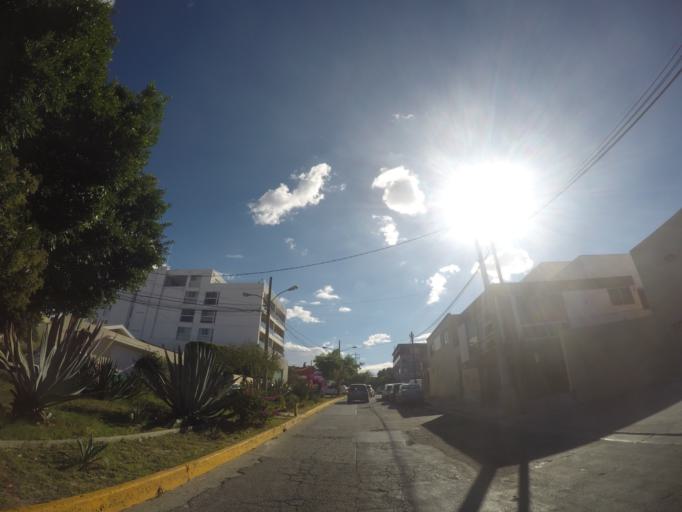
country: MX
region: San Luis Potosi
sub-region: San Luis Potosi
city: San Luis Potosi
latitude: 22.1453
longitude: -101.0194
